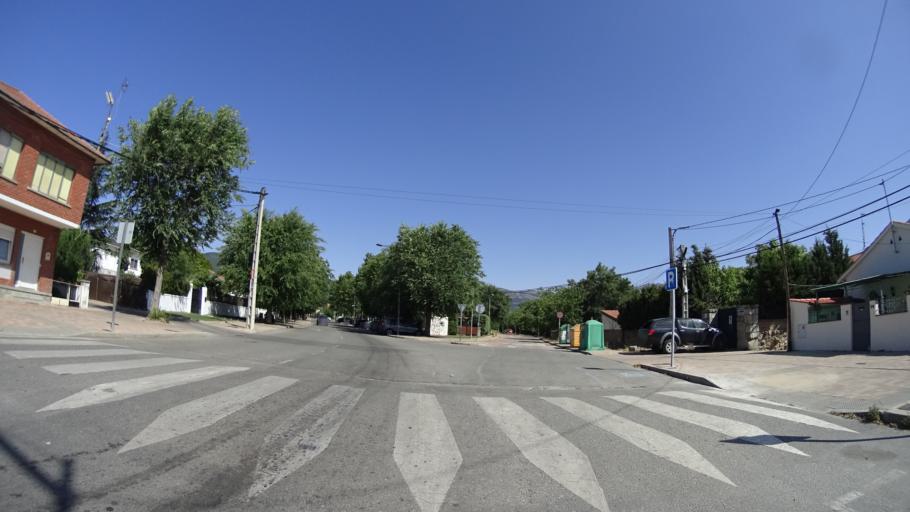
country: ES
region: Madrid
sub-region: Provincia de Madrid
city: Guadarrama
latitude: 40.6767
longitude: -4.0909
